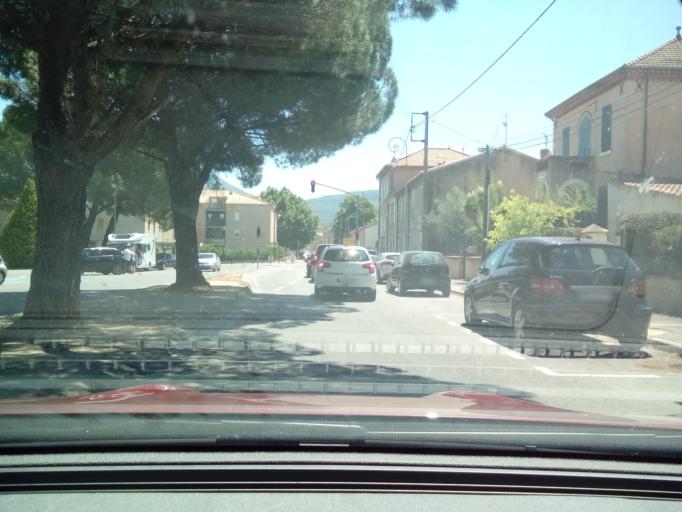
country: FR
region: Provence-Alpes-Cote d'Azur
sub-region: Departement des Bouches-du-Rhone
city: Trets
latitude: 43.4490
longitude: 5.6787
